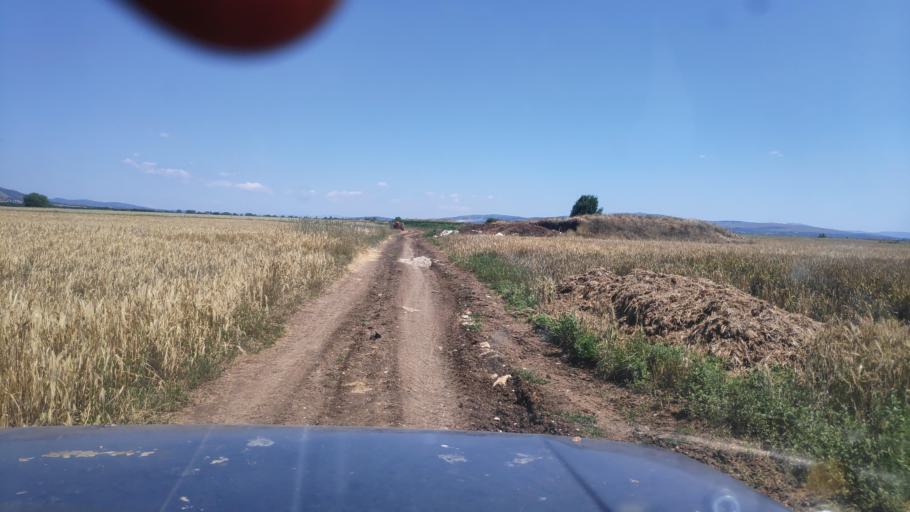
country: MK
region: Kumanovo
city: Bedinje
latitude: 42.1594
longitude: 21.6822
